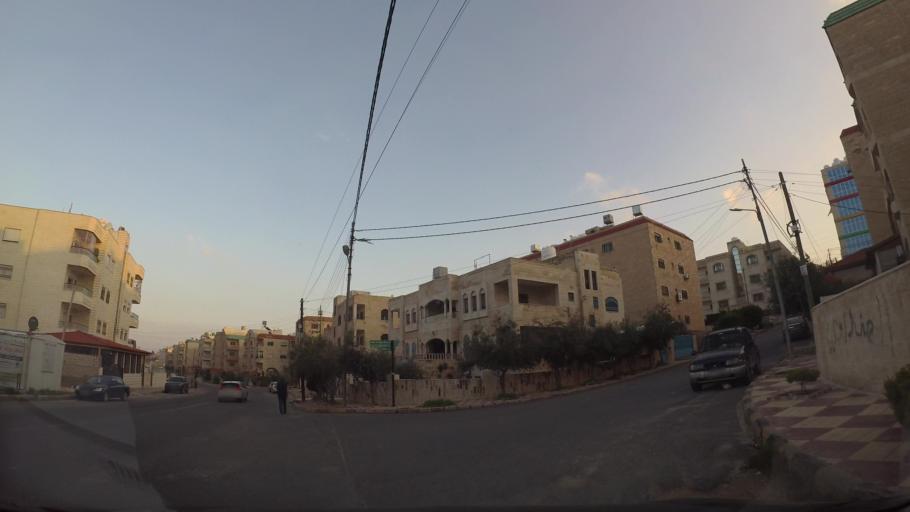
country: JO
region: Amman
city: Amman
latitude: 31.9918
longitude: 35.9478
